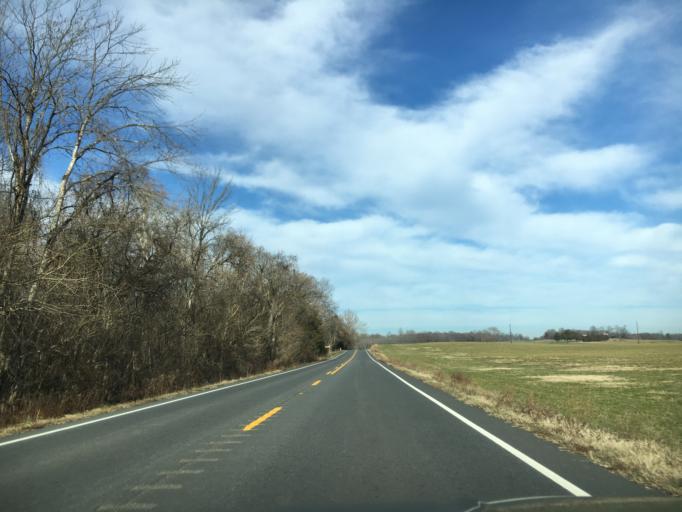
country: US
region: Virginia
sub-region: Culpeper County
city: Culpeper
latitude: 38.3345
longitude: -77.9557
